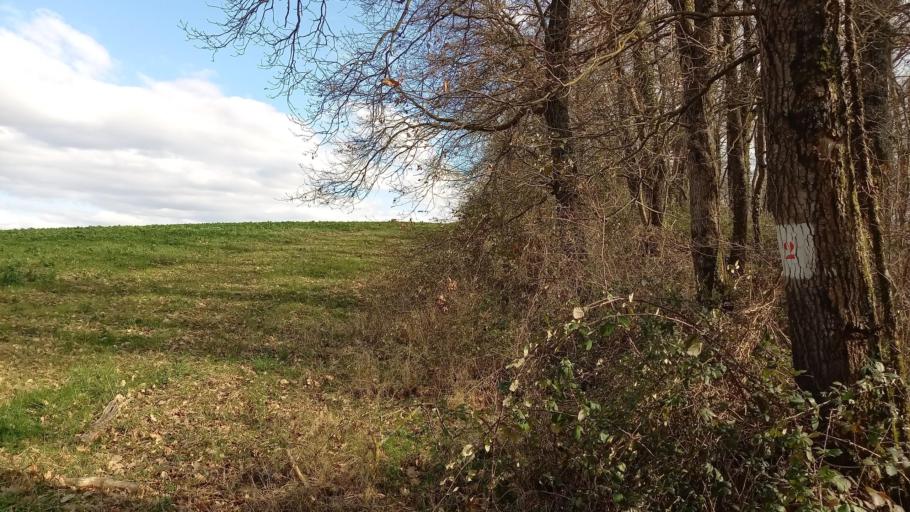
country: FR
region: Midi-Pyrenees
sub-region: Departement de la Haute-Garonne
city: Gaillac-Toulza
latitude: 43.2388
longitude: 1.5122
